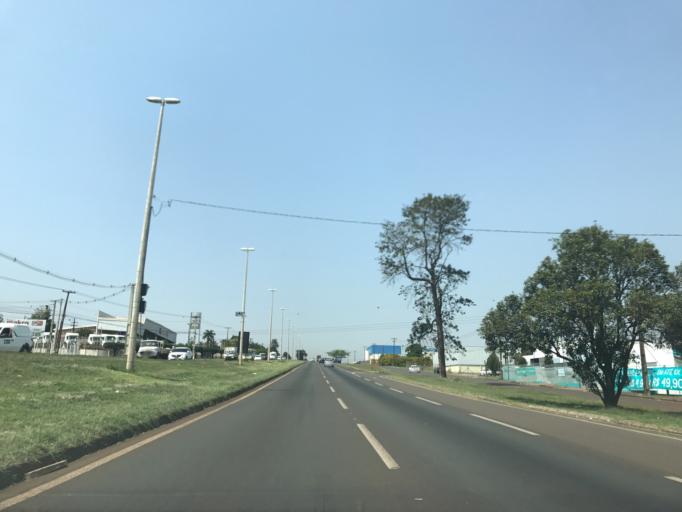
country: BR
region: Parana
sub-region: Cambe
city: Cambe
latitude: -23.2830
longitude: -51.2487
